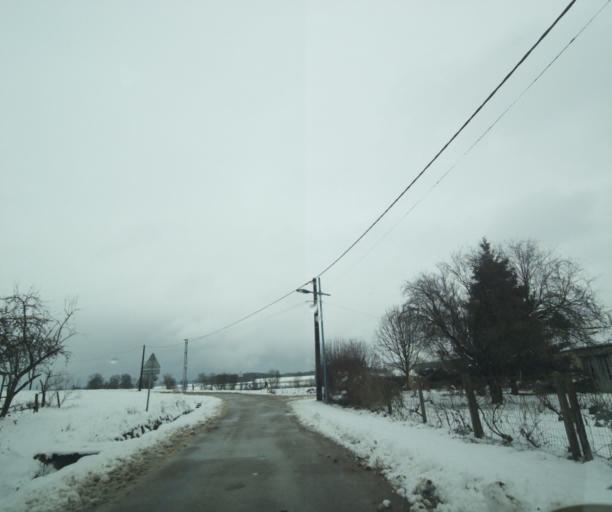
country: FR
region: Champagne-Ardenne
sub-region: Departement de la Haute-Marne
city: Montier-en-Der
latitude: 48.4227
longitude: 4.7875
